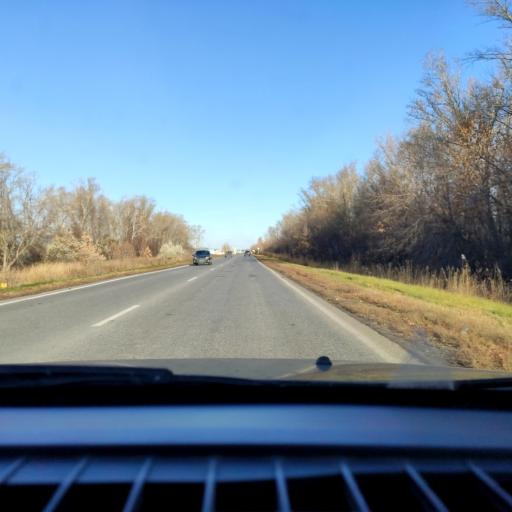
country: RU
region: Samara
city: Tol'yatti
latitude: 53.6286
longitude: 49.3044
